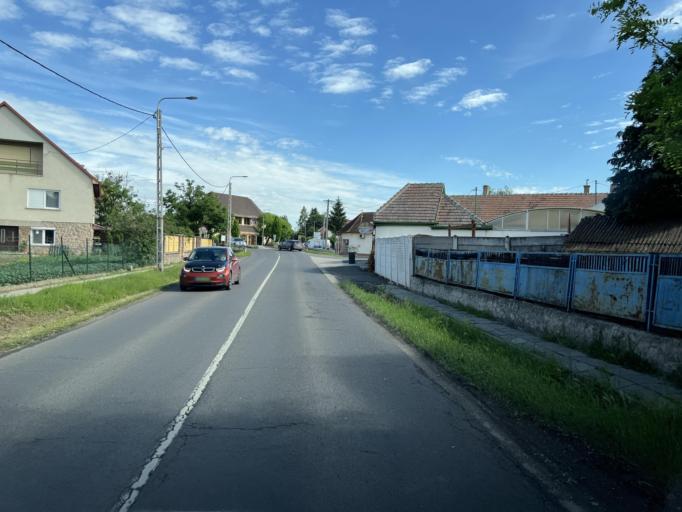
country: HU
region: Pest
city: Isaszeg
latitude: 47.5309
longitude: 19.4004
